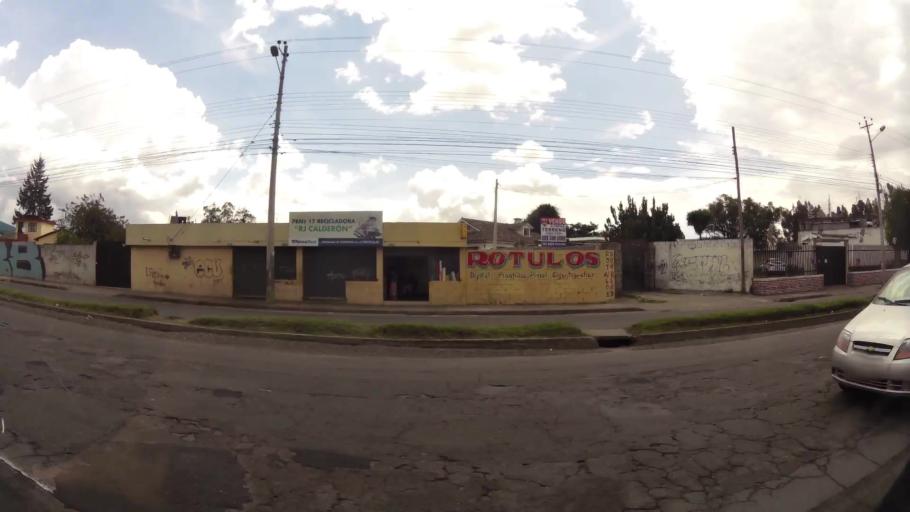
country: EC
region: Pichincha
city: Quito
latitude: -0.1053
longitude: -78.4327
